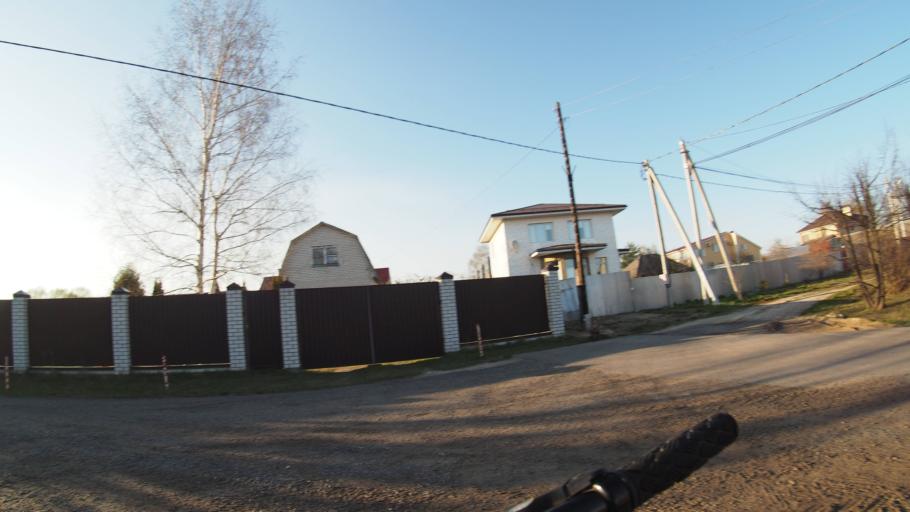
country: RU
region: Moskovskaya
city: Malyshevo
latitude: 55.4968
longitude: 38.3470
